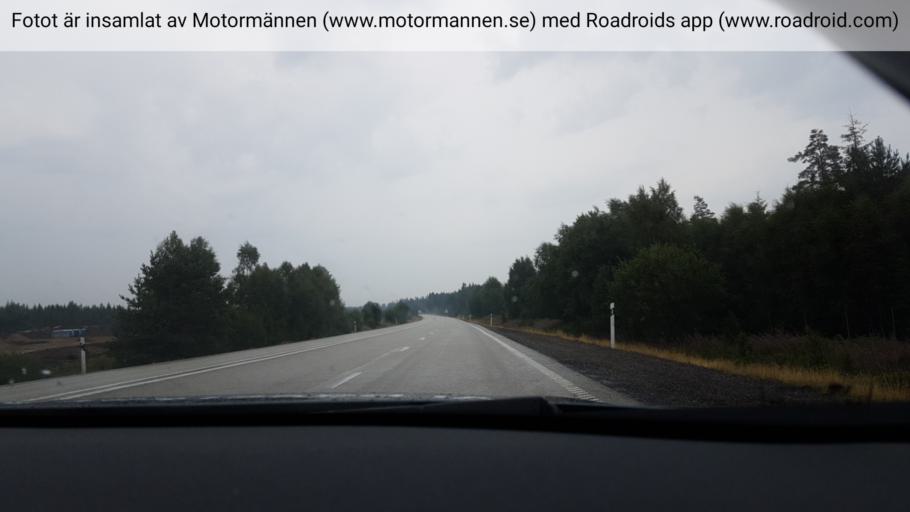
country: SE
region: Joenkoeping
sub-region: Jonkopings Kommun
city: Odensjo
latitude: 57.6236
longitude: 14.1879
